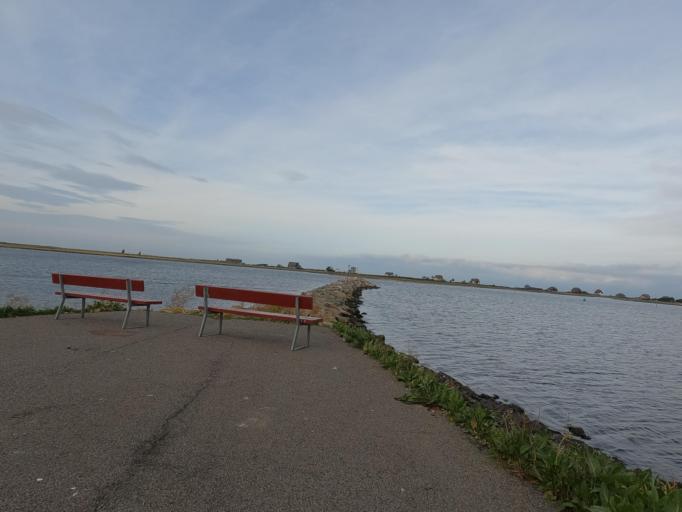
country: DE
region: Schleswig-Holstein
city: Heiligenhafen
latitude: 54.3731
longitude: 10.9917
